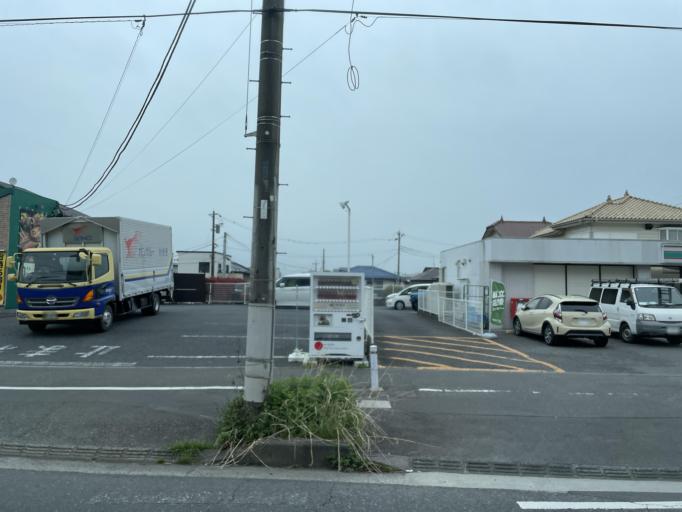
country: JP
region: Saitama
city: Saitama
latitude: 35.8713
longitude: 139.7000
